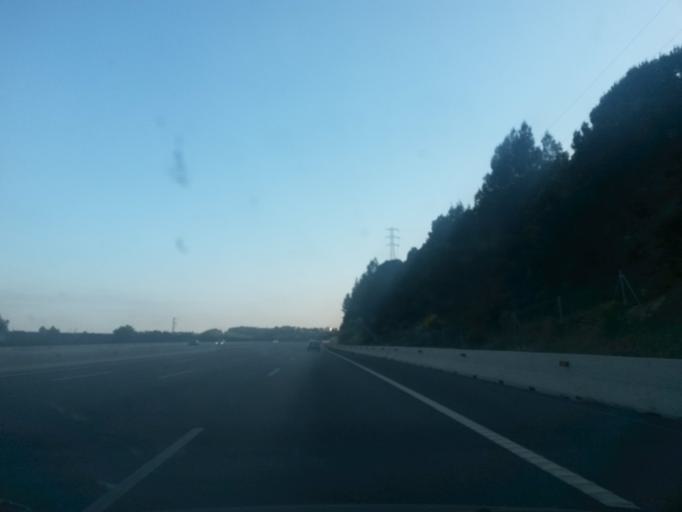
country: ES
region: Catalonia
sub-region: Provincia de Girona
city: Sarria de Ter
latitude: 42.0182
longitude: 2.8146
